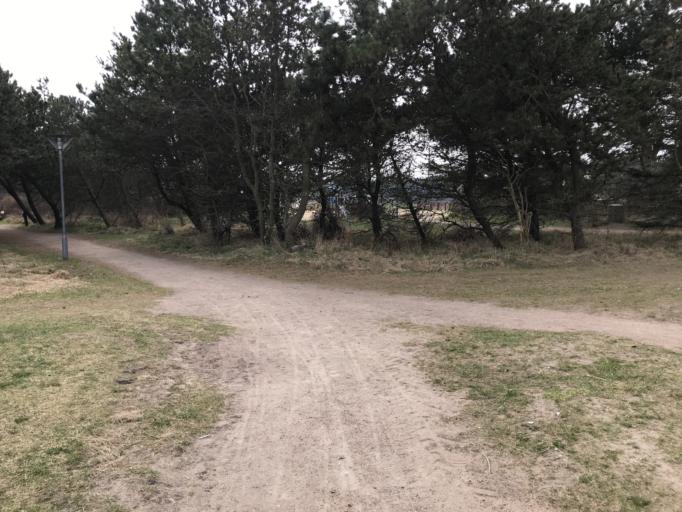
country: DK
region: North Denmark
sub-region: Hjorring Kommune
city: Hjorring
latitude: 57.4929
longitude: 9.8375
